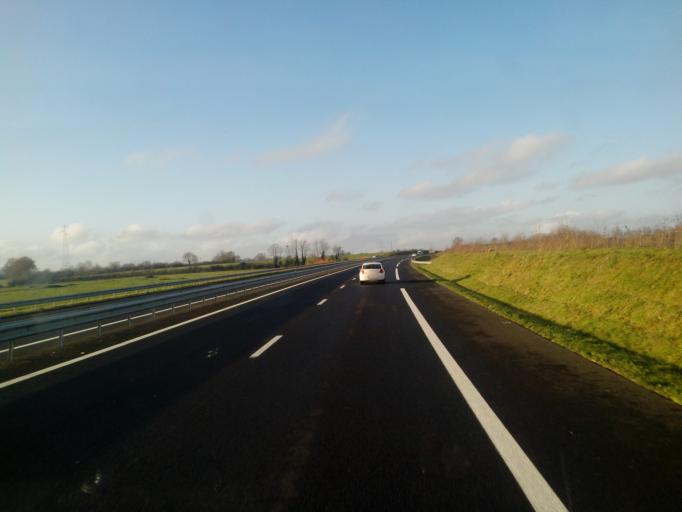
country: FR
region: Pays de la Loire
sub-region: Departement de Maine-et-Loire
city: La Tessoualle
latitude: 46.9979
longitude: -0.8603
